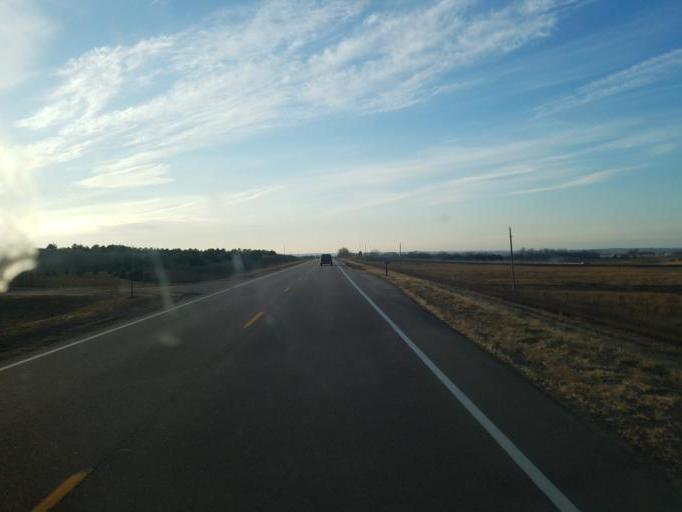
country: US
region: South Dakota
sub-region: Yankton County
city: Yankton
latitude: 42.7288
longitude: -97.4518
